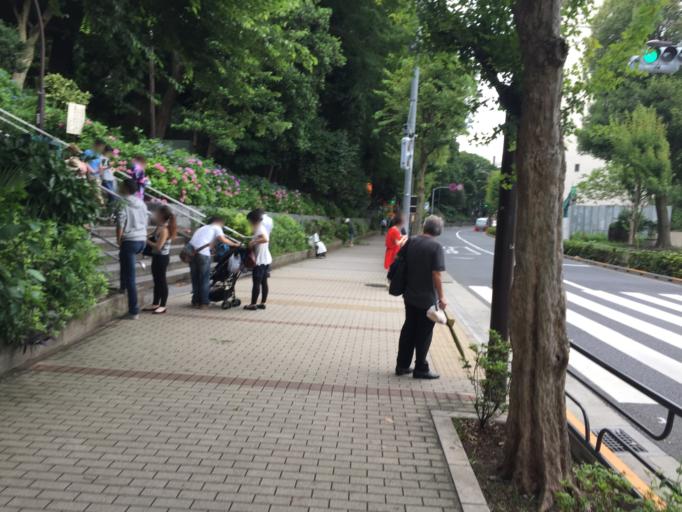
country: JP
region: Tokyo
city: Tokyo
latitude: 35.7125
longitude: 139.7727
